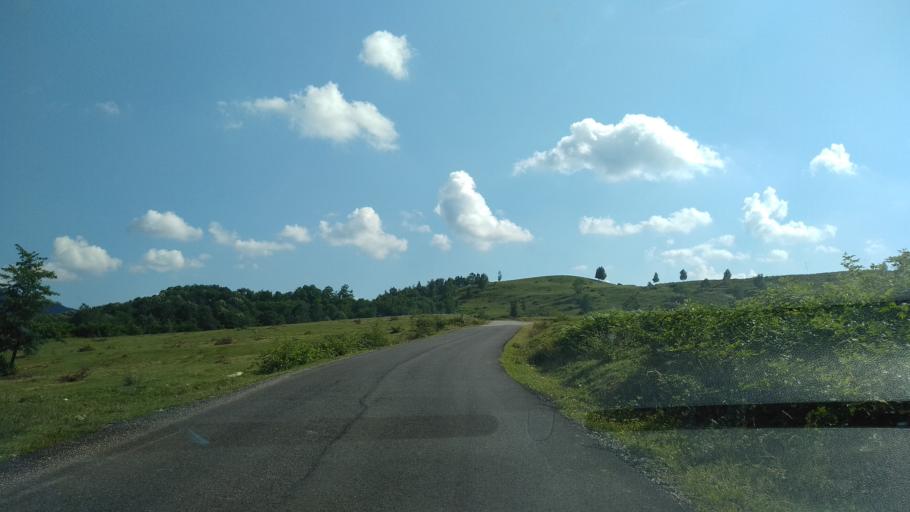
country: RO
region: Hunedoara
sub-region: Comuna Orastioara de Sus
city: Orastioara de Sus
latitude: 45.7186
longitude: 23.1602
